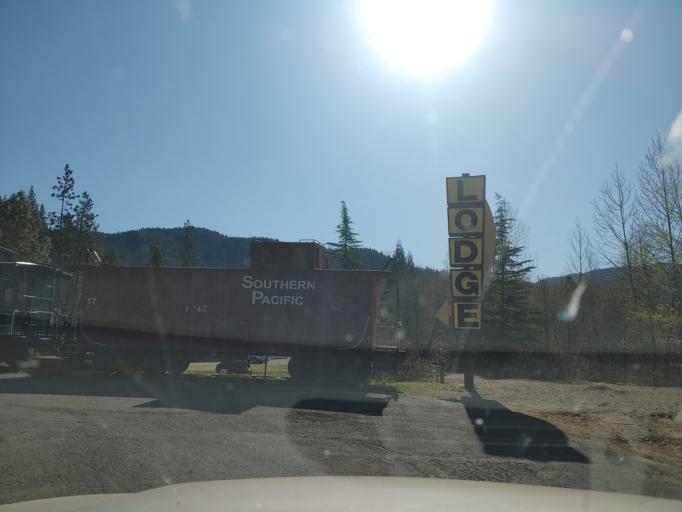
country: US
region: California
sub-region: Siskiyou County
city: Dunsmuir
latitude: 41.1848
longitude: -122.2933
